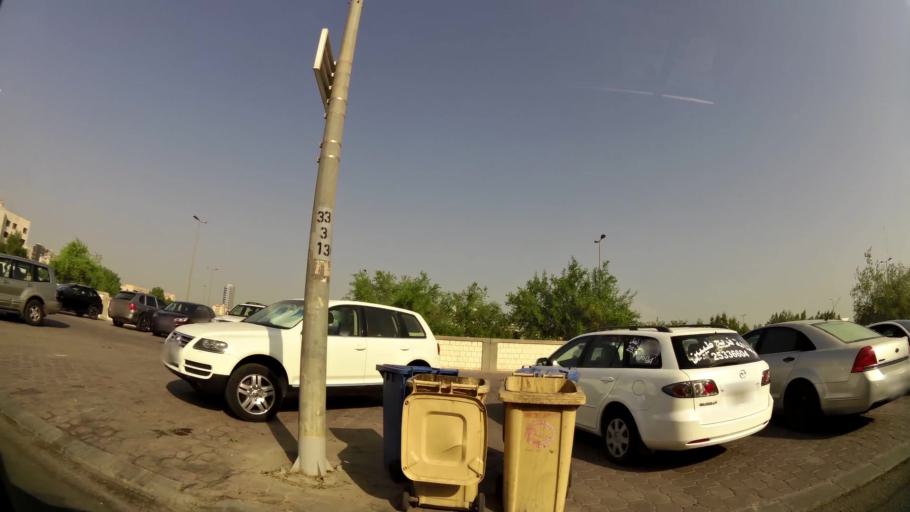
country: KW
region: Muhafazat Hawalli
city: Hawalli
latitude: 29.3239
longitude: 48.0320
